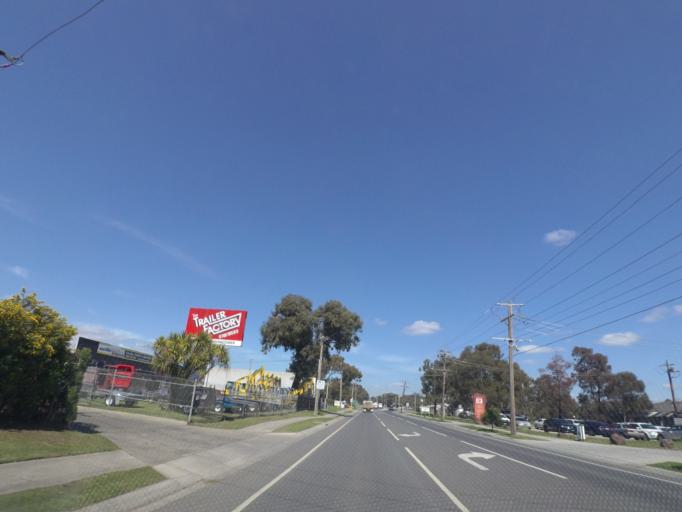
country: AU
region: Victoria
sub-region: Maroondah
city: Bayswater North
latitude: -37.8192
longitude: 145.3047
